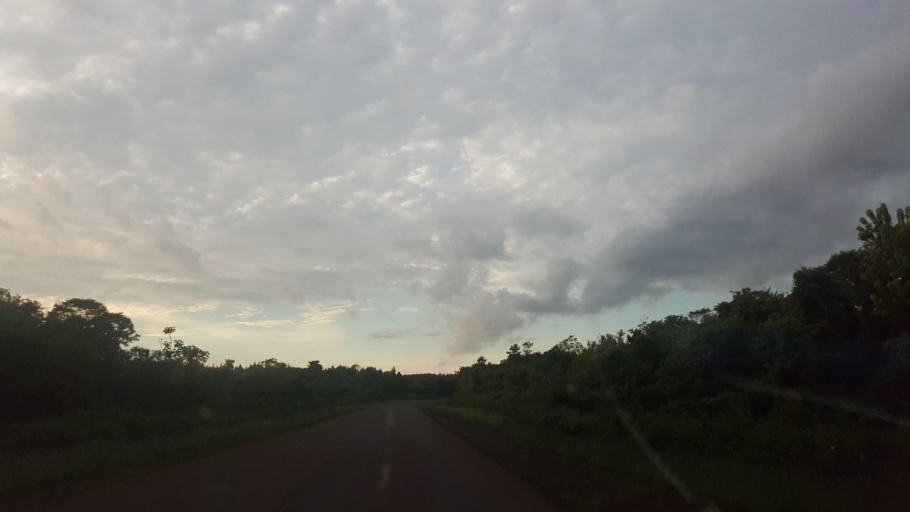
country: AR
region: Misiones
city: Dos de Mayo
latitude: -26.9293
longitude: -54.7201
